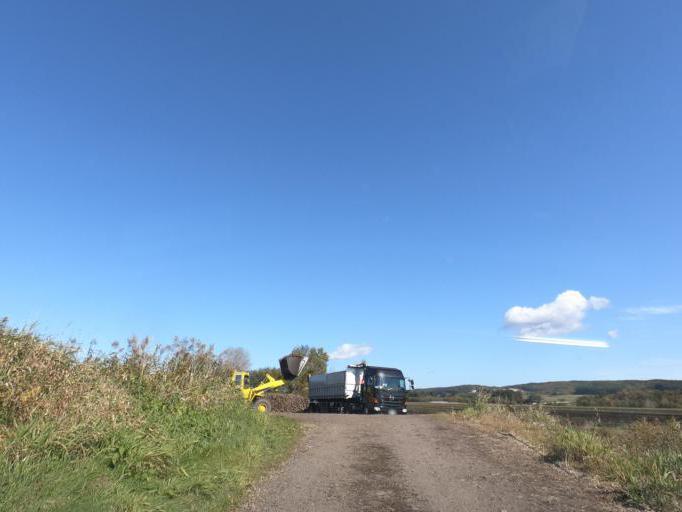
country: JP
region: Hokkaido
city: Otofuke
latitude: 43.0640
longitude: 143.2790
